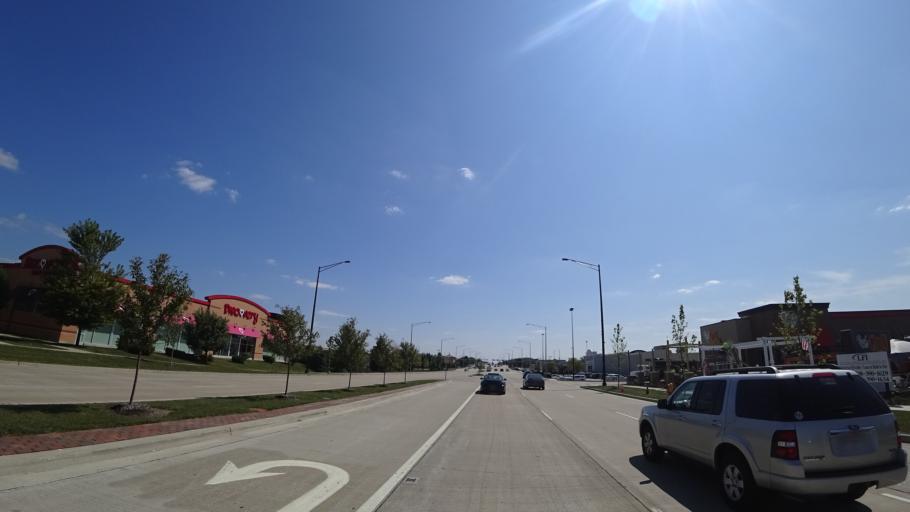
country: US
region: Illinois
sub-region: Cook County
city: Orland Hills
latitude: 41.6058
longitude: -87.8531
